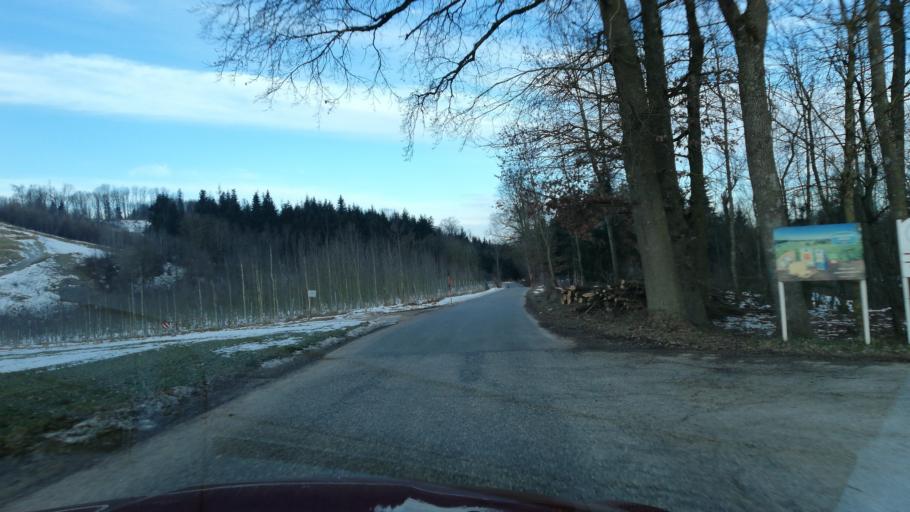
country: AT
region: Upper Austria
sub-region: Wels-Land
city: Buchkirchen
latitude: 48.2344
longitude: 13.9950
